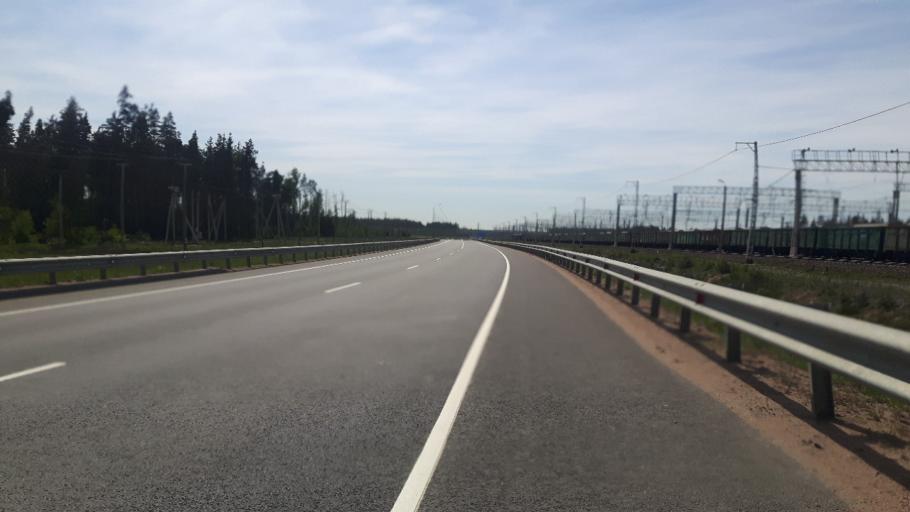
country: RU
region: Leningrad
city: Vistino
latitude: 59.6696
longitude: 28.4327
